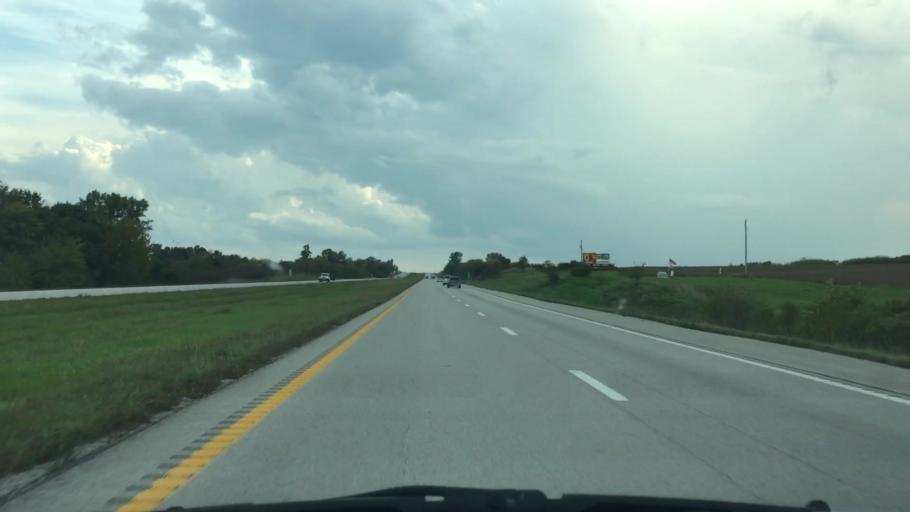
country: US
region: Missouri
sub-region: Clinton County
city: Cameron
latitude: 39.8211
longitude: -94.1914
